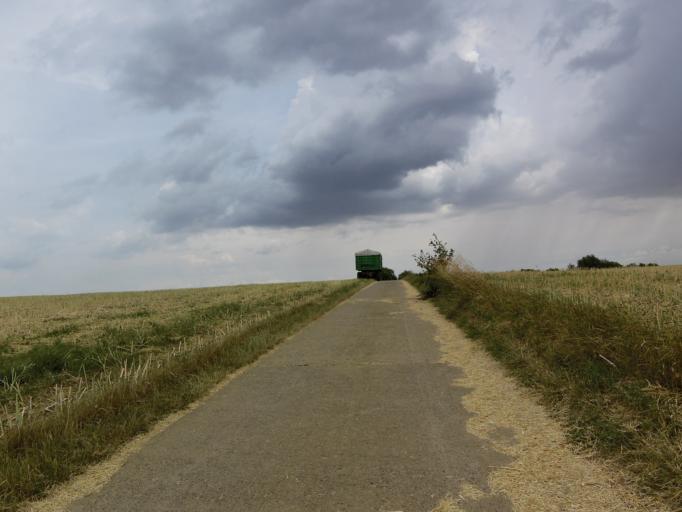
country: DE
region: Bavaria
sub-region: Regierungsbezirk Unterfranken
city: Randersacker
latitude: 49.7677
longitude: 9.9783
